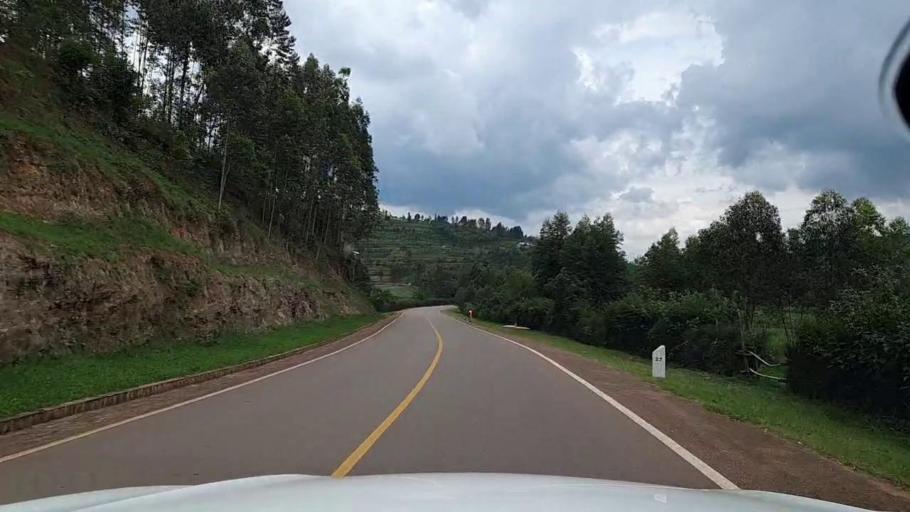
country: RW
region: Kigali
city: Kigali
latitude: -1.7959
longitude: 30.1288
